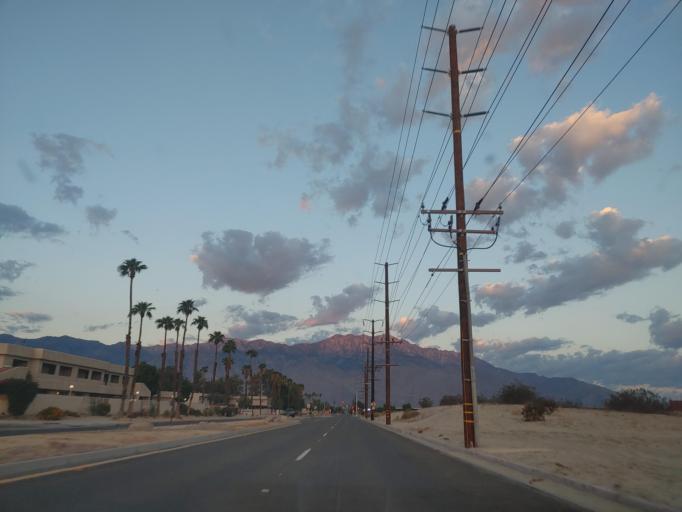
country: US
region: California
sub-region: Riverside County
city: Cathedral City
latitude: 33.8016
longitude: -116.4462
